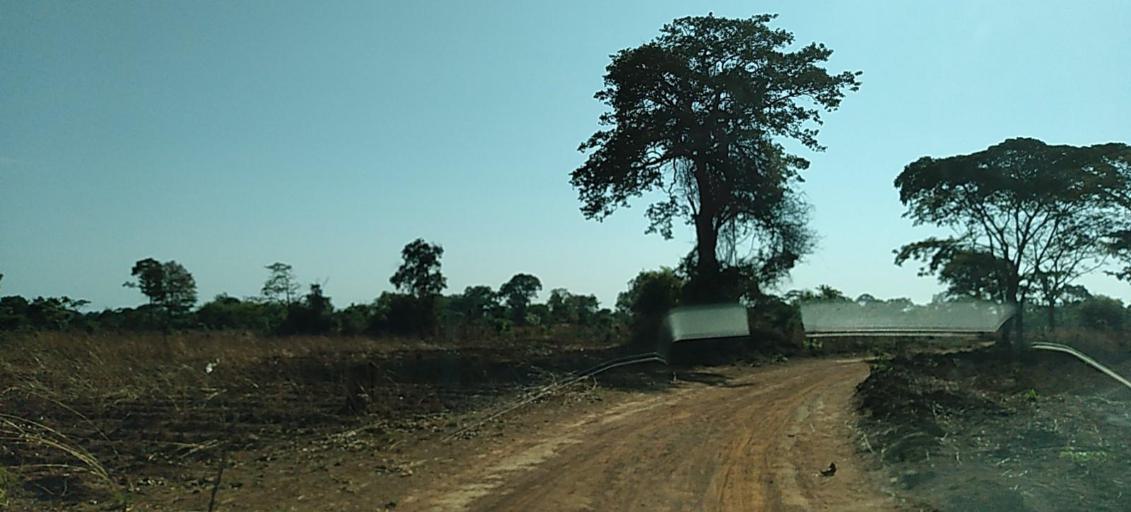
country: ZM
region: Copperbelt
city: Chililabombwe
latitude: -12.3692
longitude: 27.9149
